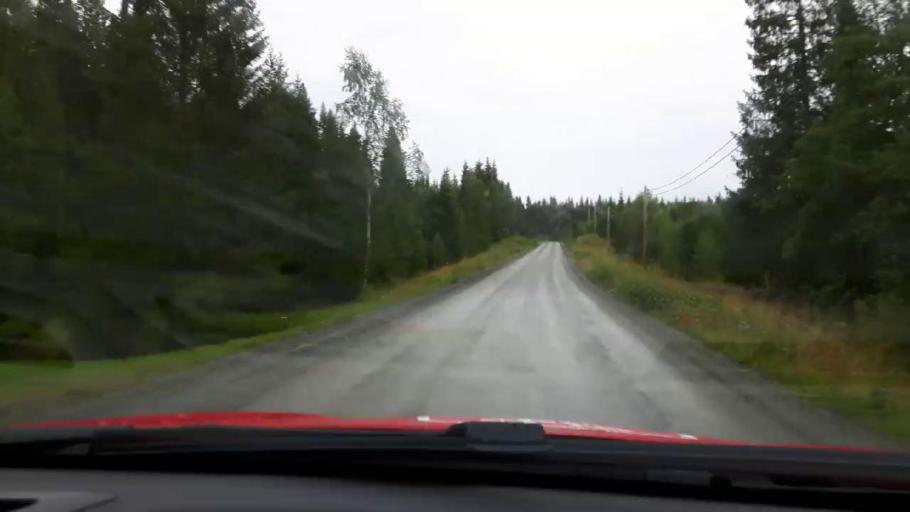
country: SE
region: Jaemtland
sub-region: Are Kommun
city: Are
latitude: 63.4820
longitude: 12.7951
